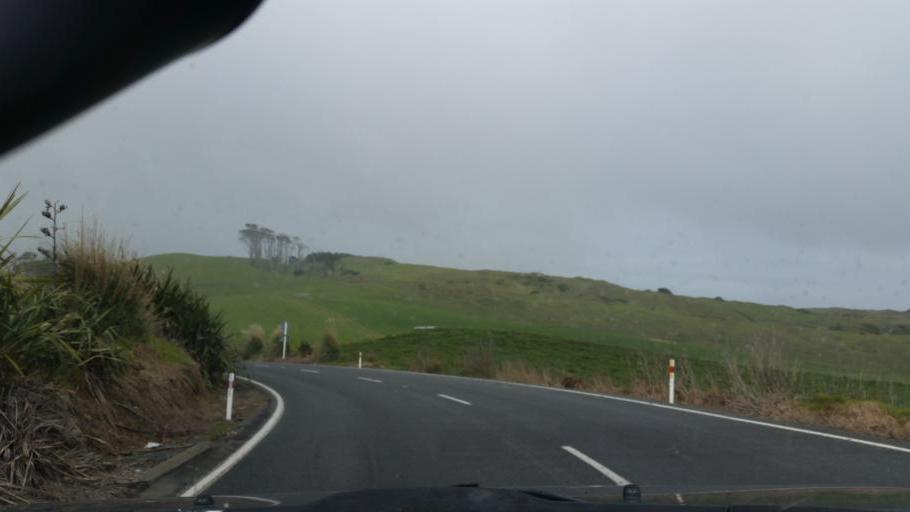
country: NZ
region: Northland
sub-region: Kaipara District
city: Dargaville
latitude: -36.0684
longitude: 173.8625
